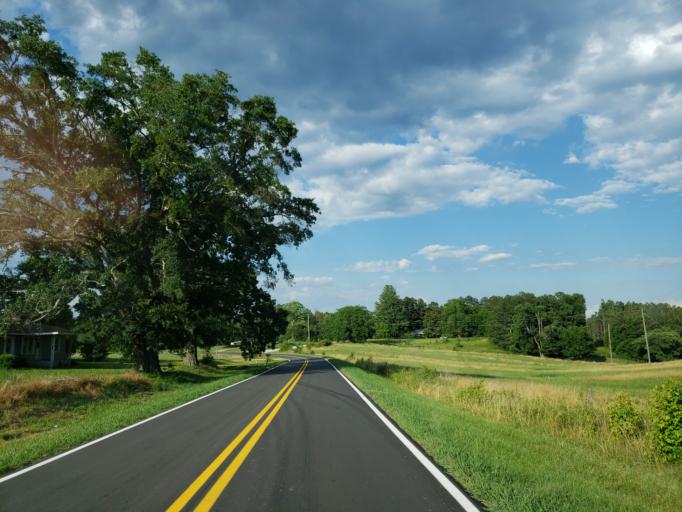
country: US
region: Georgia
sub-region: Haralson County
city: Buchanan
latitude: 33.8330
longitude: -85.2041
